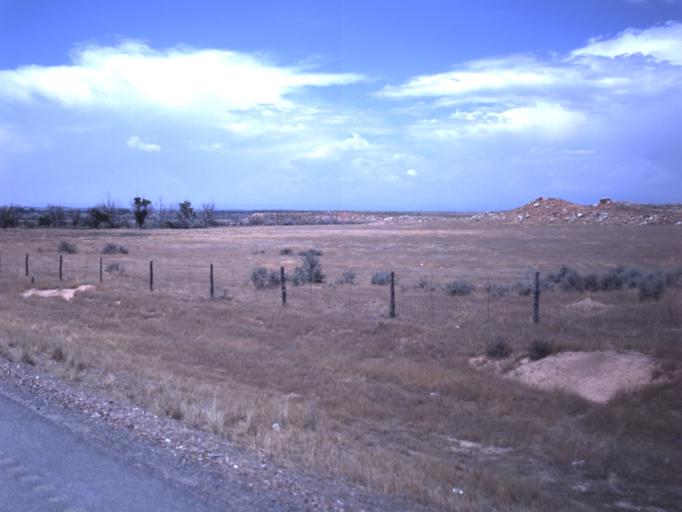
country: US
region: Utah
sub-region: Duchesne County
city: Roosevelt
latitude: 40.3055
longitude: -109.7689
